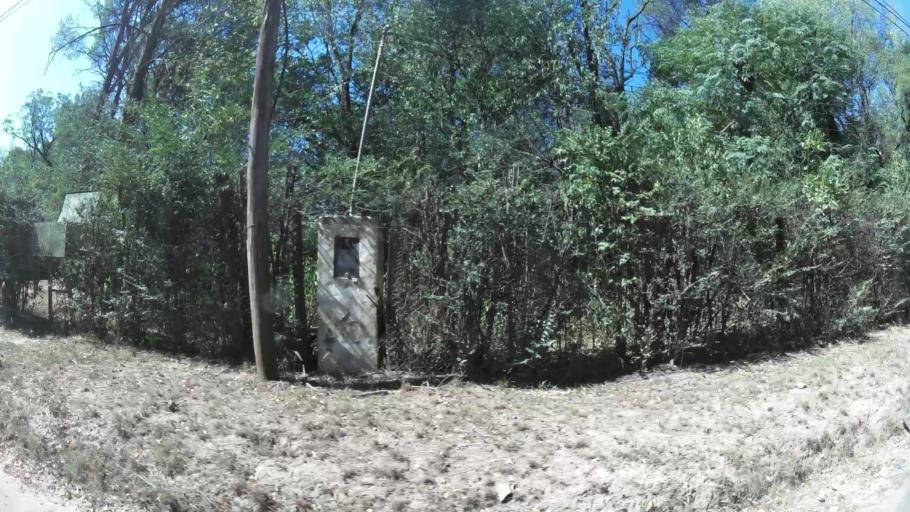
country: AR
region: Cordoba
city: Mendiolaza
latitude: -31.2731
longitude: -64.2958
